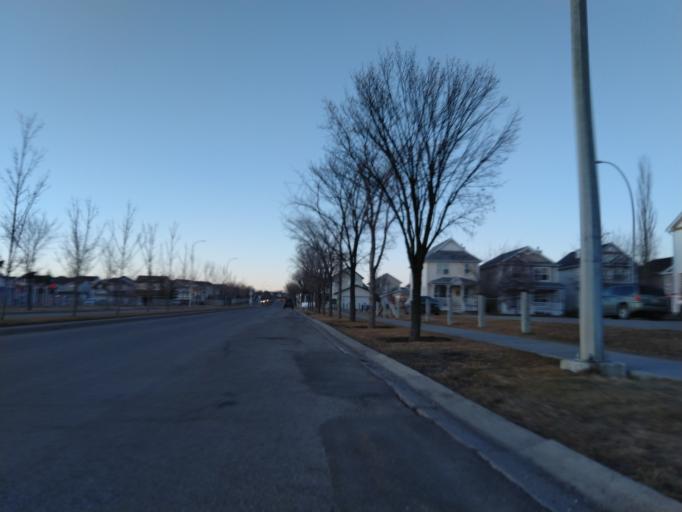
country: CA
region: Alberta
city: Calgary
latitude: 51.1280
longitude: -114.2492
